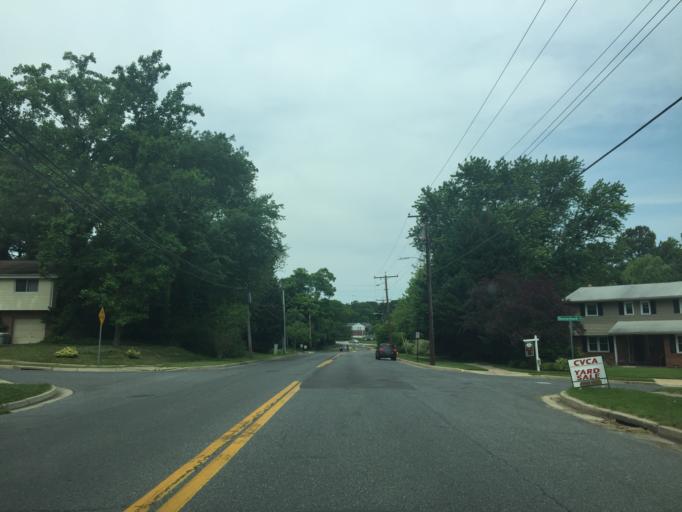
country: US
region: Maryland
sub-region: Baltimore County
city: Towson
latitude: 39.4014
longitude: -76.5833
